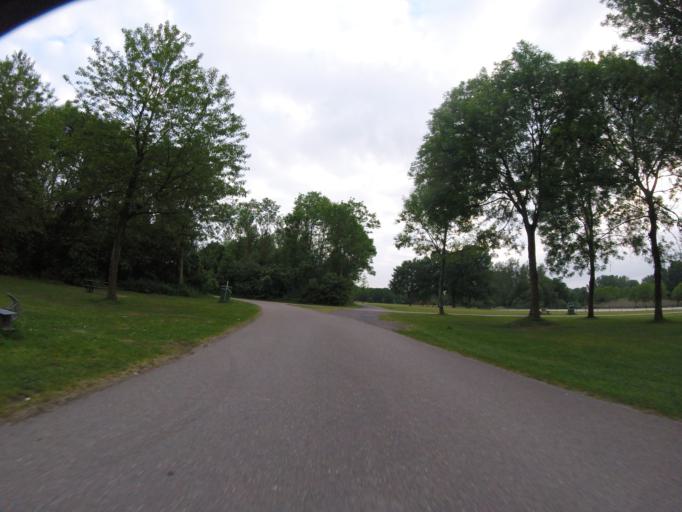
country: NL
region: North Holland
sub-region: Gemeente Haarlemmermeer
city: Hoofddorp
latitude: 52.3239
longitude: 4.6712
